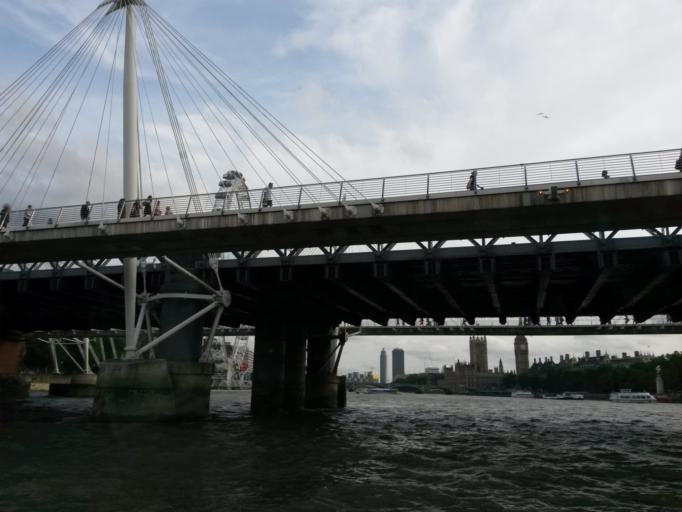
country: GB
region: England
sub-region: Greater London
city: London
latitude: 51.5066
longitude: -0.1199
